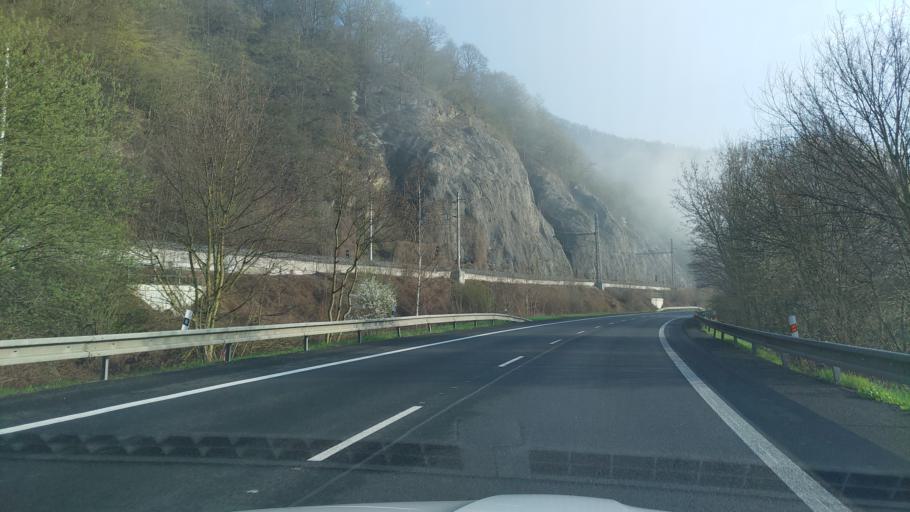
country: CZ
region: Ustecky
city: Povrly
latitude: 50.6788
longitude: 14.1663
